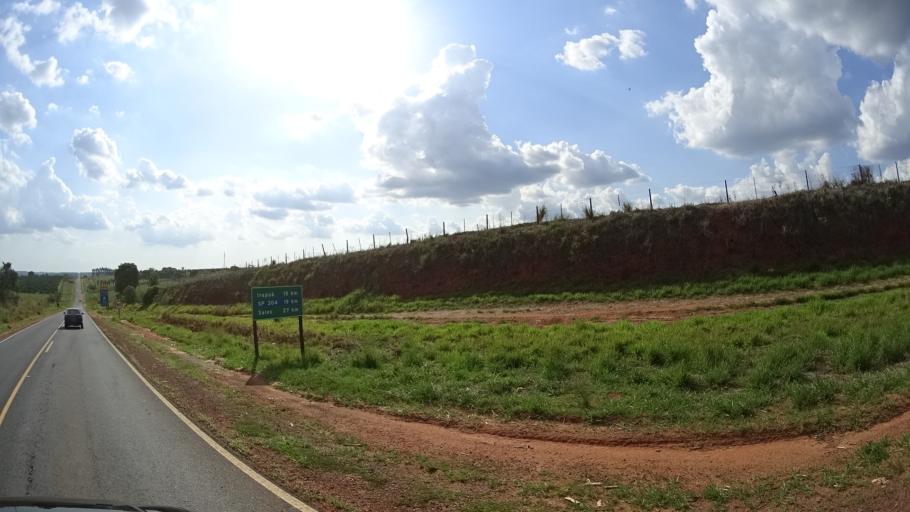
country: BR
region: Sao Paulo
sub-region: Urupes
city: Urupes
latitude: -21.1866
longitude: -49.2976
